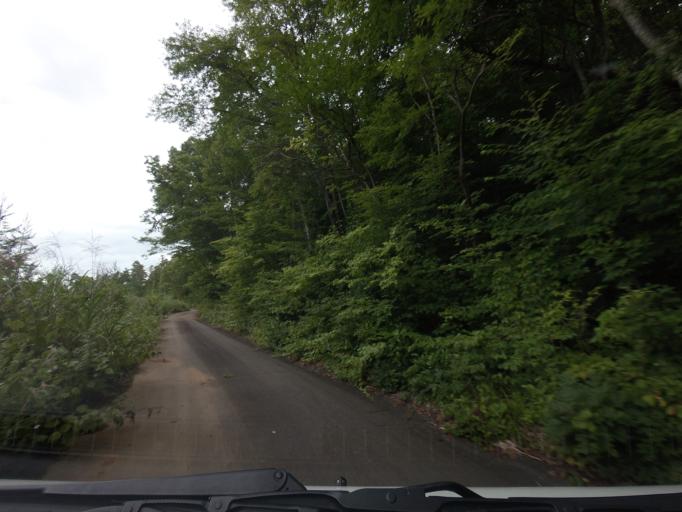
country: JP
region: Fukushima
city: Motomiya
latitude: 37.5661
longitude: 140.3066
